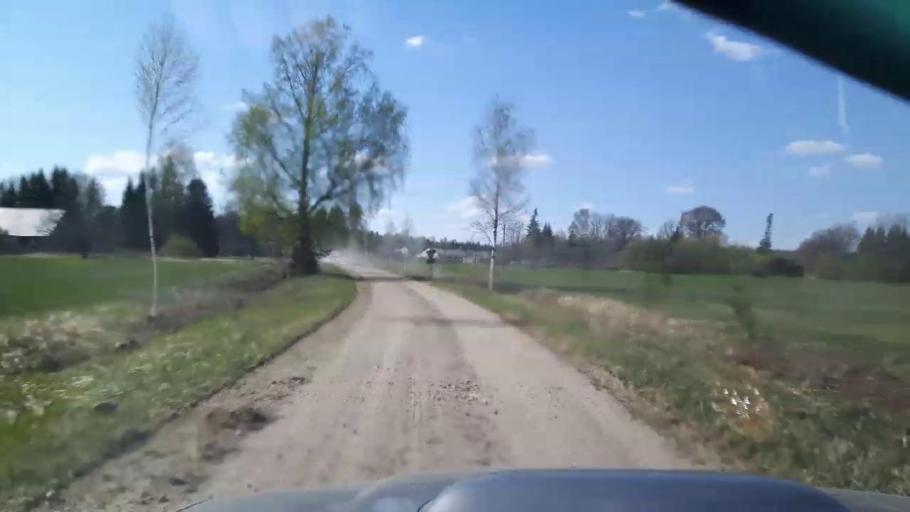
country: EE
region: Paernumaa
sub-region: Tootsi vald
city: Tootsi
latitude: 58.4486
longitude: 24.8619
